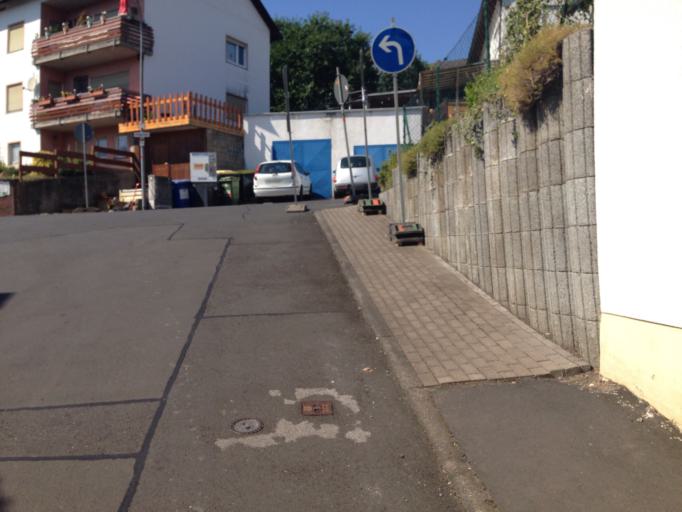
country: DE
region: Hesse
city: Beuern
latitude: 50.6691
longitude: 8.7905
